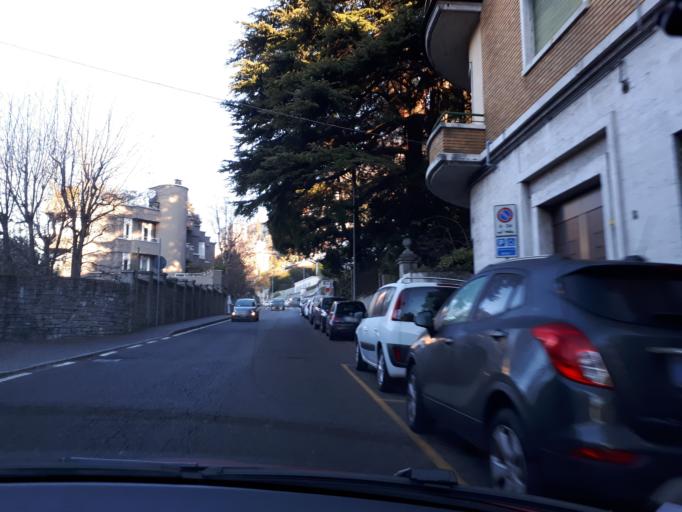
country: IT
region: Lombardy
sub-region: Provincia di Como
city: Brunate
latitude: 45.8164
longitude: 9.0845
